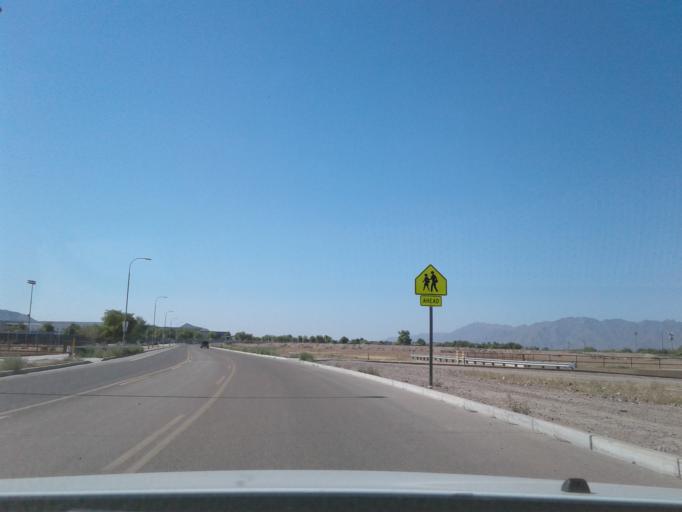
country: US
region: Arizona
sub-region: Maricopa County
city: Laveen
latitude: 33.3758
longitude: -112.1851
